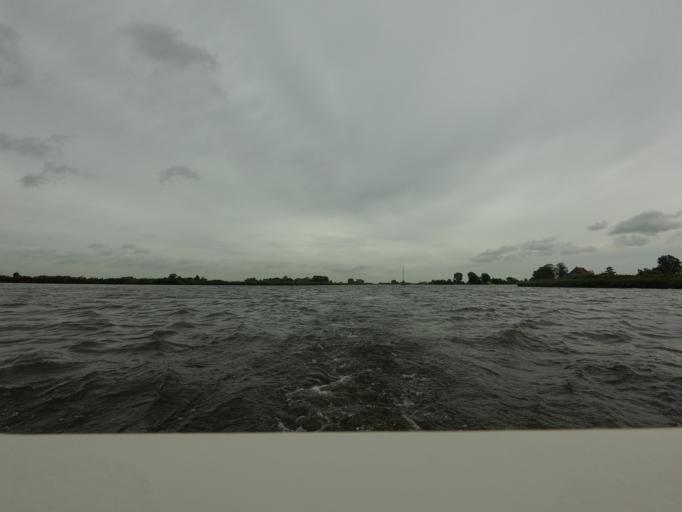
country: NL
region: Friesland
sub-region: Gemeente Boarnsterhim
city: Grou
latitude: 53.1035
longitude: 5.8529
